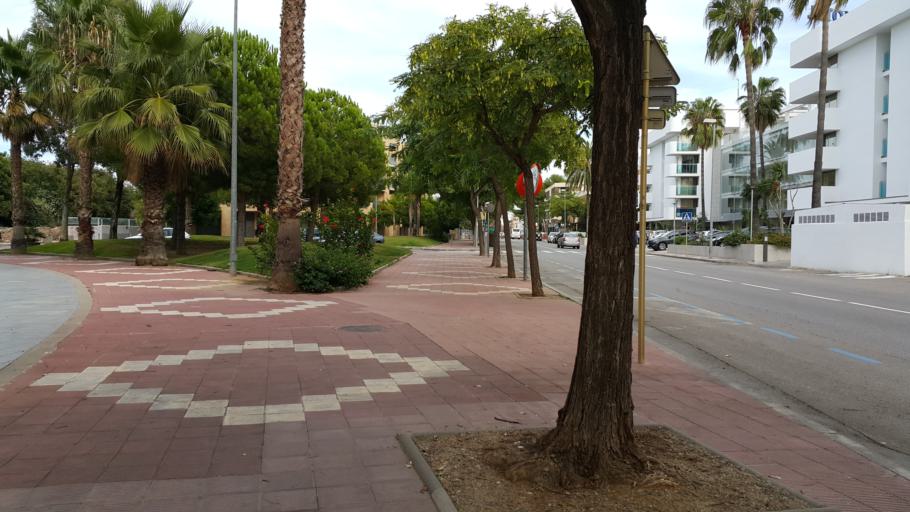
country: ES
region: Catalonia
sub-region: Provincia de Tarragona
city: Salou
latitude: 41.0733
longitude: 1.1108
